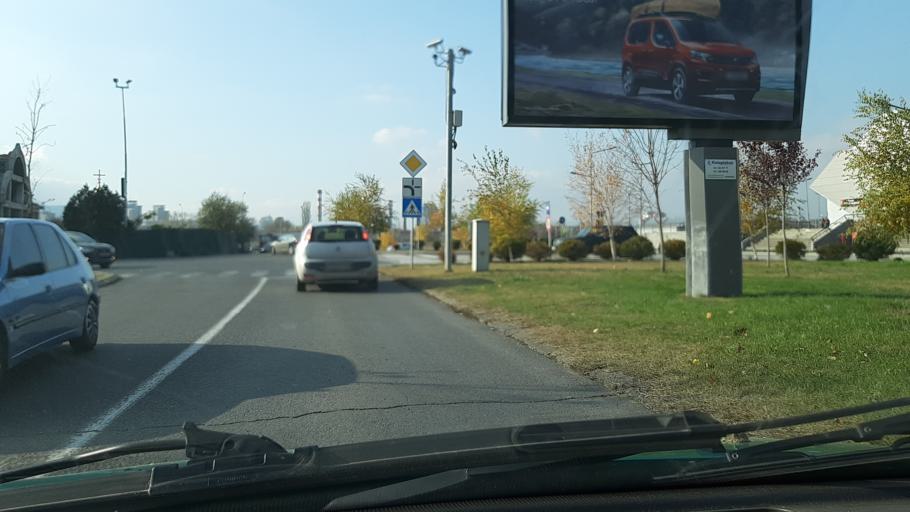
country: MK
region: Cair
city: Cair
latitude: 41.9923
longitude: 21.4655
